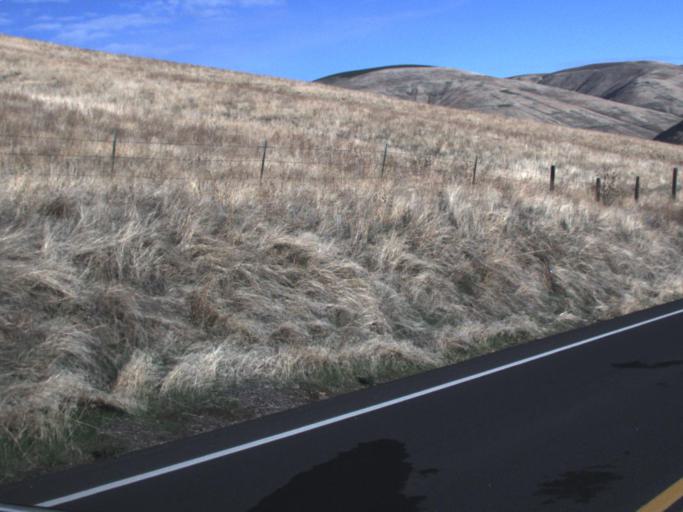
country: US
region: Washington
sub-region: Whitman County
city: Colfax
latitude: 46.7119
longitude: -117.4725
